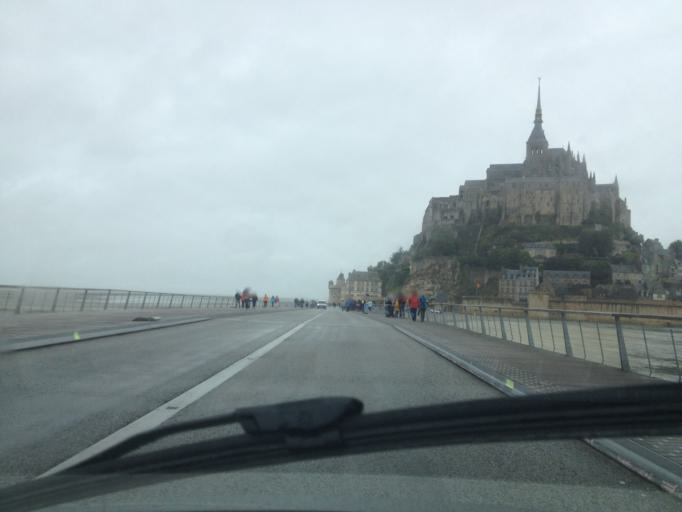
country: FR
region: Lower Normandy
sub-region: Departement de la Manche
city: Pontorson
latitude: 48.6325
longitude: -1.5092
